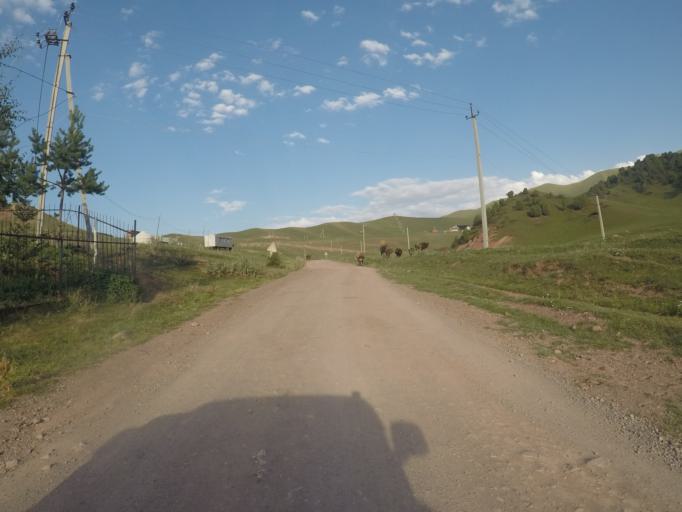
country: KG
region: Chuy
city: Bishkek
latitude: 42.6412
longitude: 74.6214
